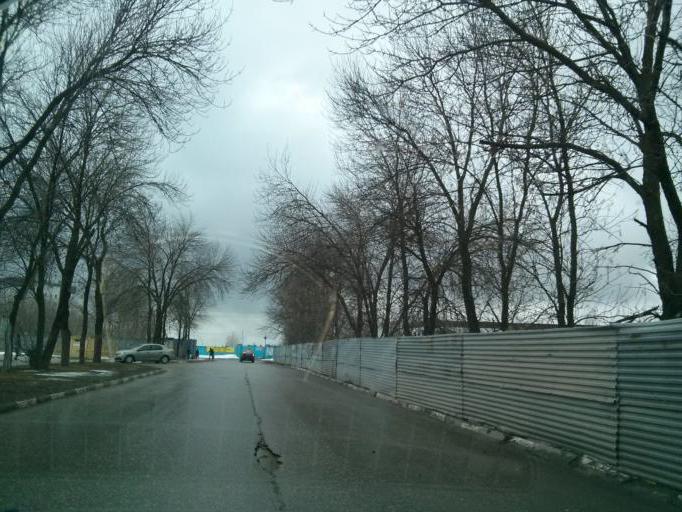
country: RU
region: Nizjnij Novgorod
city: Bor
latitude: 56.3084
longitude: 44.0721
